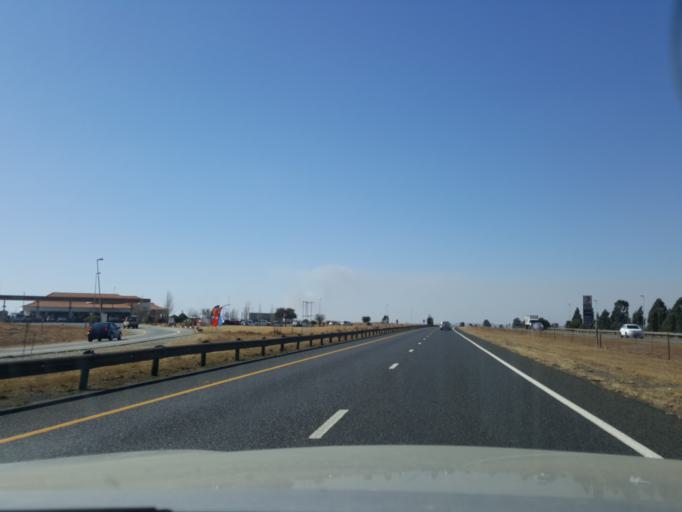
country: ZA
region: Mpumalanga
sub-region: Nkangala District Municipality
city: Delmas
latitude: -26.0454
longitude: 28.8310
